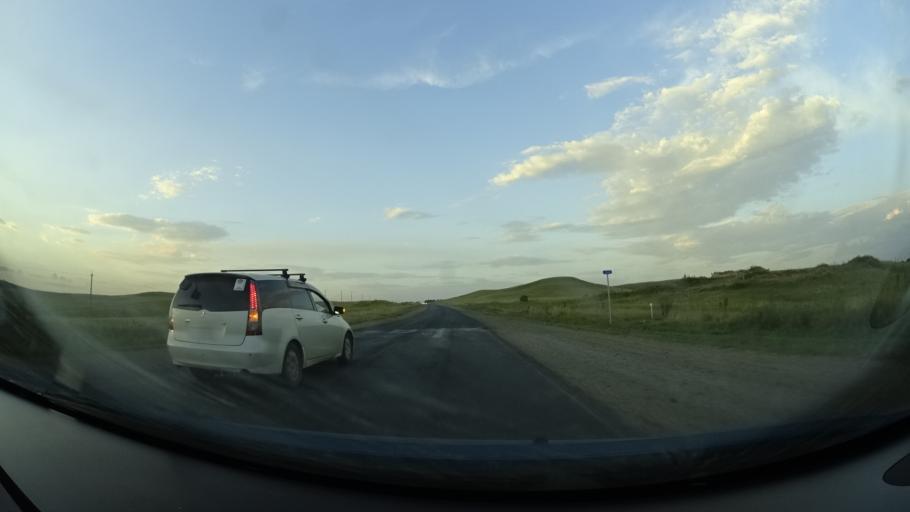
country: RU
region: Orenburg
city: Severnoye
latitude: 54.1355
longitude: 52.5956
